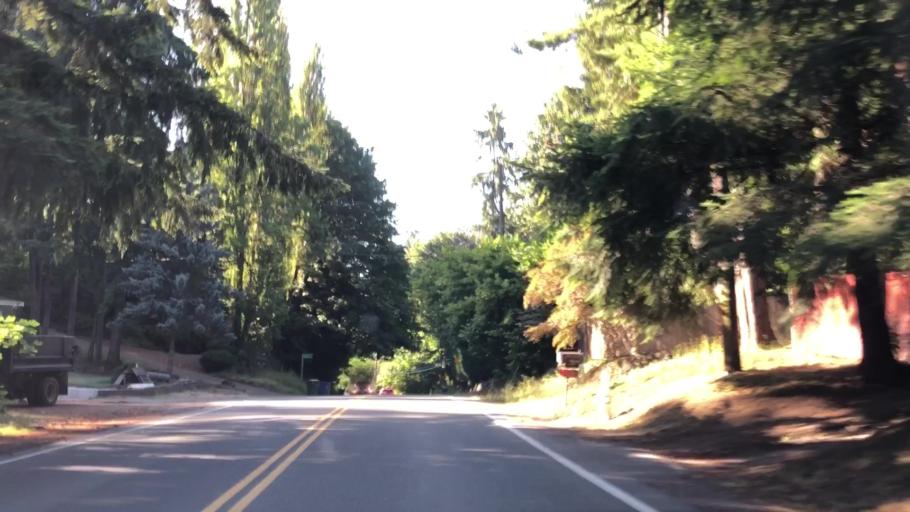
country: US
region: Washington
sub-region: King County
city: Lake Forest Park
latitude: 47.7709
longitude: -122.2859
